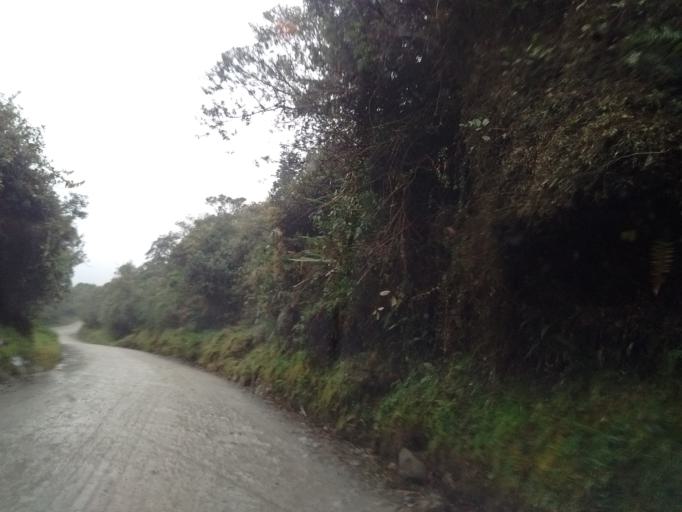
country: CO
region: Cauca
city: Paispamba
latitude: 2.1473
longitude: -76.4305
